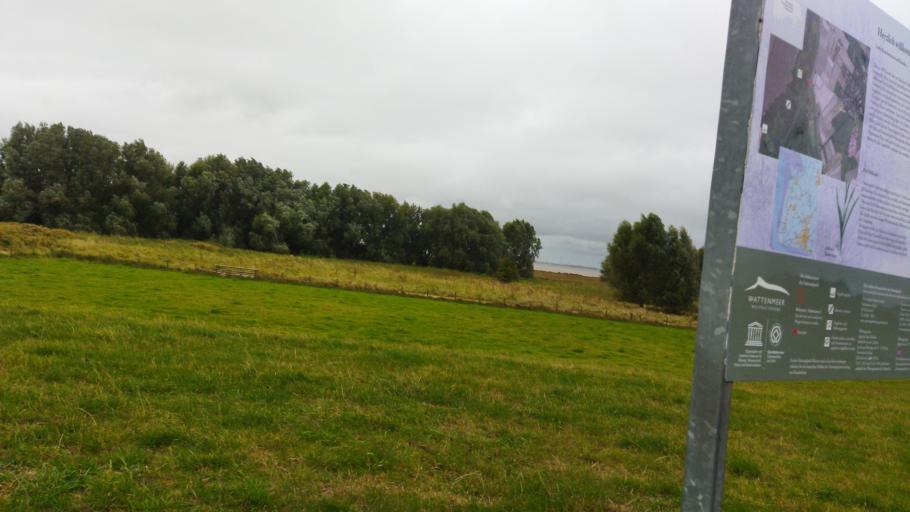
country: NL
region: Groningen
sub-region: Gemeente Delfzijl
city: Delfzijl
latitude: 53.3790
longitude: 7.0150
